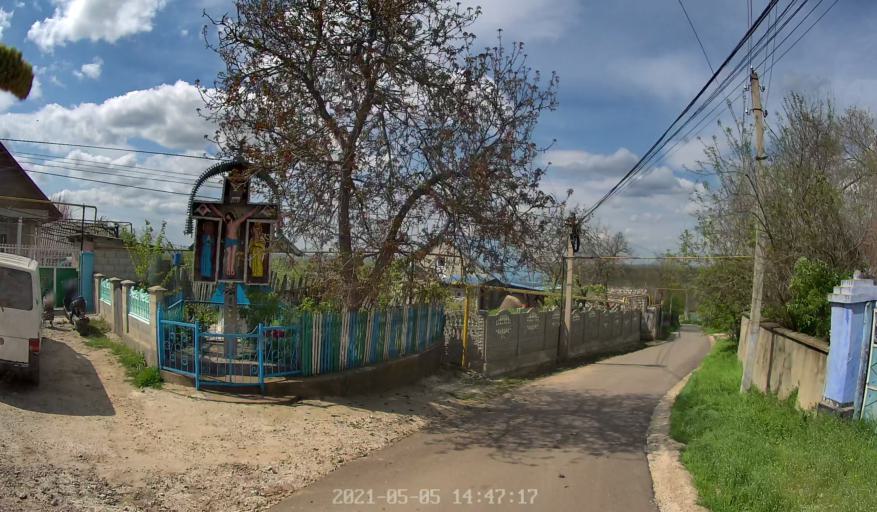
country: MD
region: Chisinau
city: Vadul lui Voda
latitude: 47.0969
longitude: 29.1700
